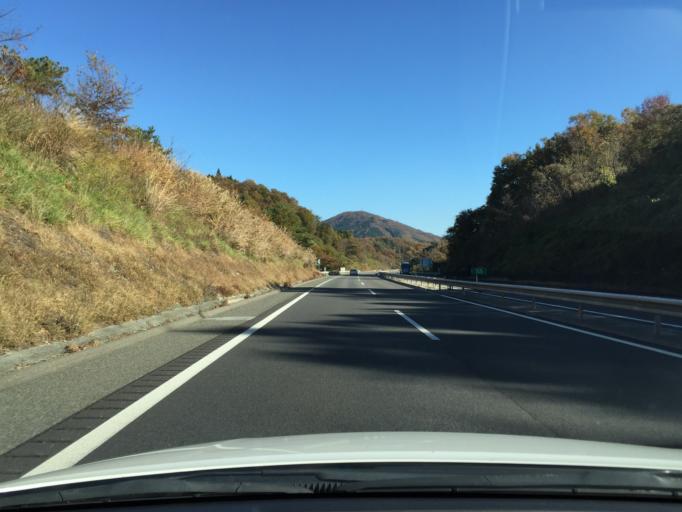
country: JP
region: Fukushima
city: Miharu
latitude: 37.4373
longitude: 140.5293
